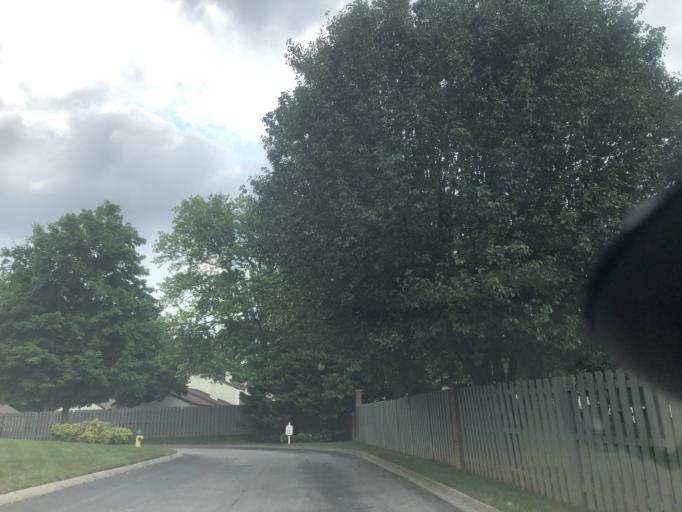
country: US
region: Tennessee
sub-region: Wilson County
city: Green Hill
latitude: 36.2440
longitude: -86.5849
